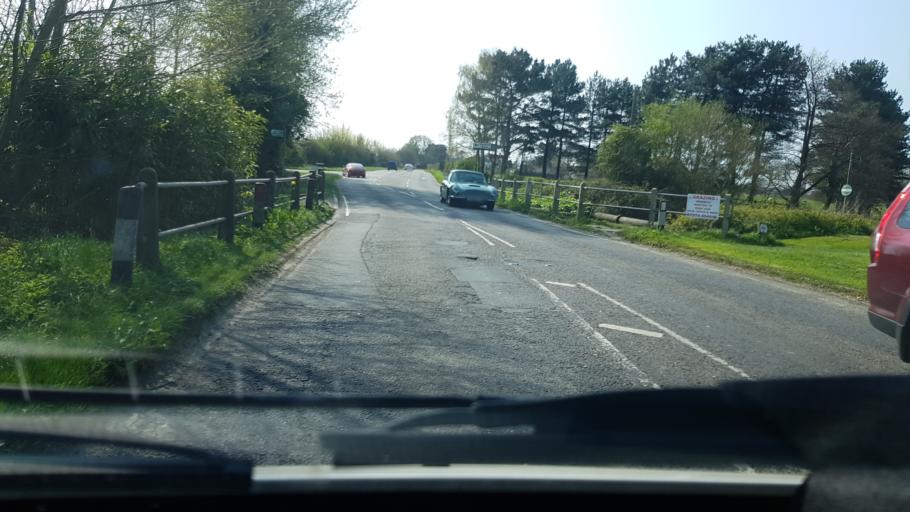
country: GB
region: England
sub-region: West Sussex
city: Birdham
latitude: 50.8053
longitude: -0.8064
